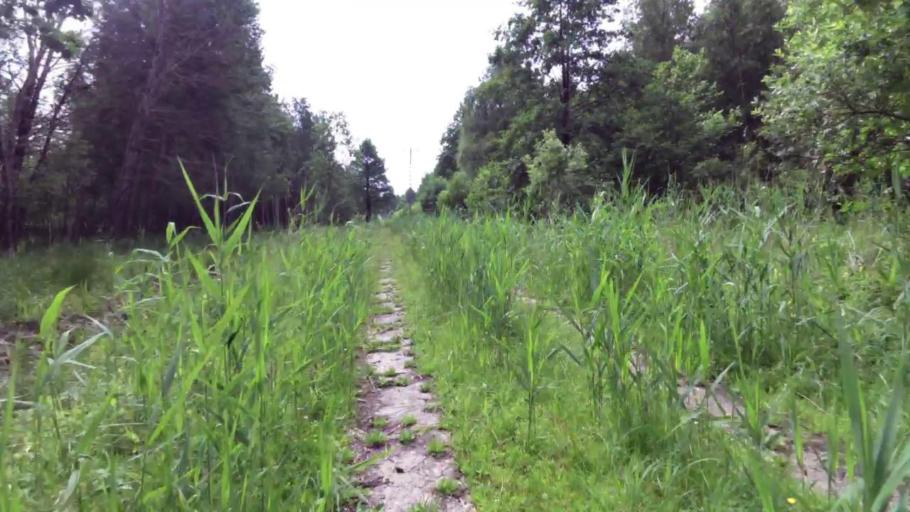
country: PL
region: West Pomeranian Voivodeship
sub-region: Powiat goleniowski
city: Stepnica
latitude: 53.7340
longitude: 14.6025
